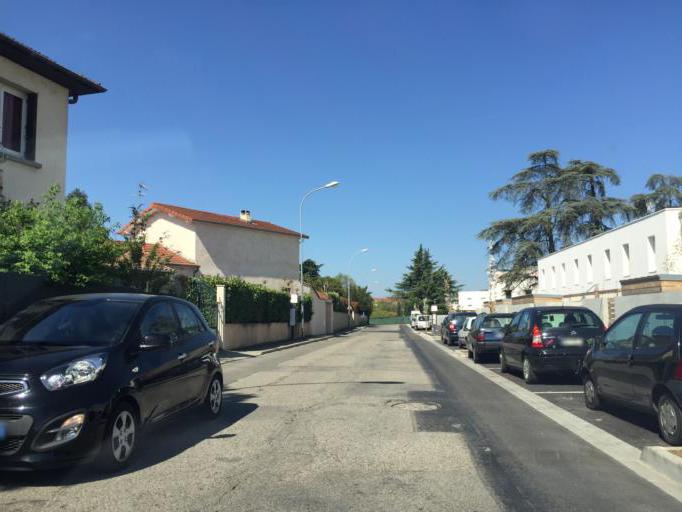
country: FR
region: Rhone-Alpes
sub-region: Departement de la Drome
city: Romans-sur-Isere
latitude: 45.0349
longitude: 5.0521
